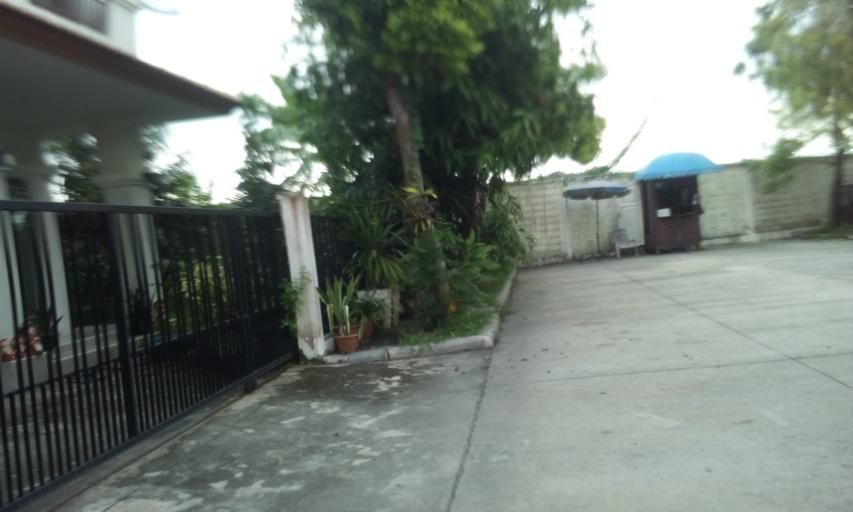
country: TH
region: Pathum Thani
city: Ban Rangsit
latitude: 14.0380
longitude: 100.8279
